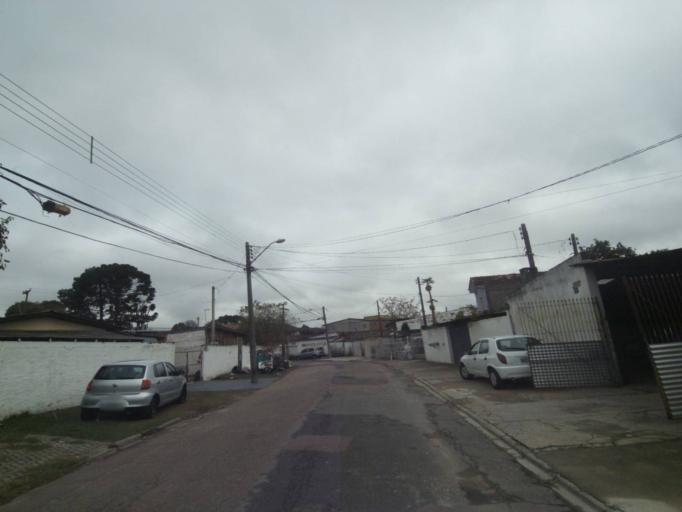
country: BR
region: Parana
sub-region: Curitiba
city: Curitiba
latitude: -25.5042
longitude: -49.2858
